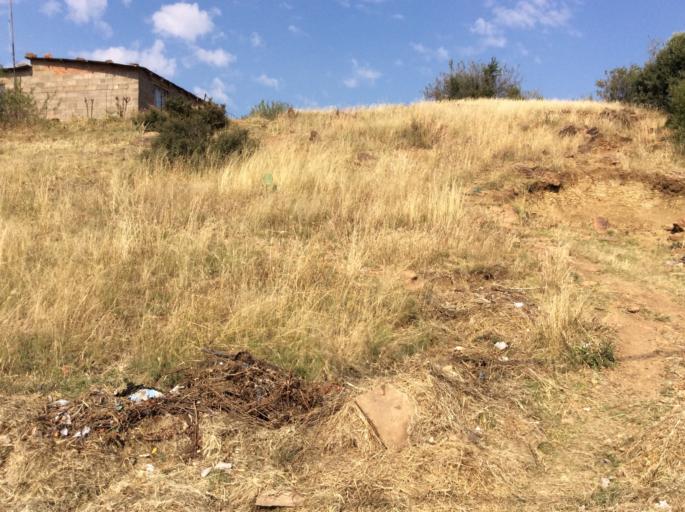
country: LS
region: Mafeteng
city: Mafeteng
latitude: -29.9816
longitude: 27.0048
